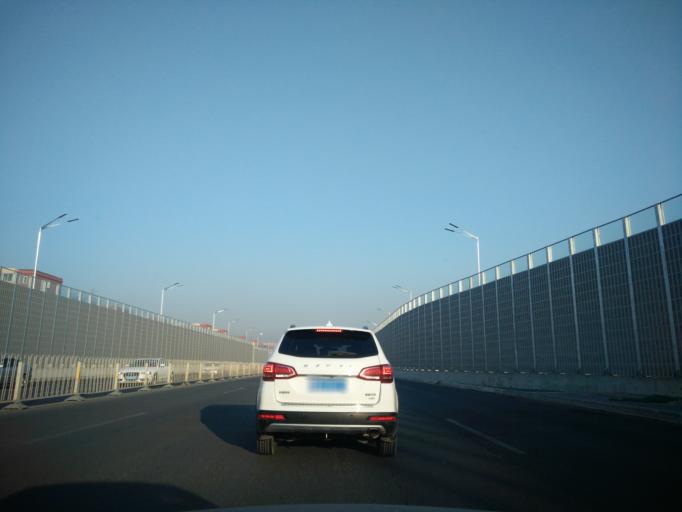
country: CN
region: Beijing
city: Jiugong
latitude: 39.7934
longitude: 116.4781
